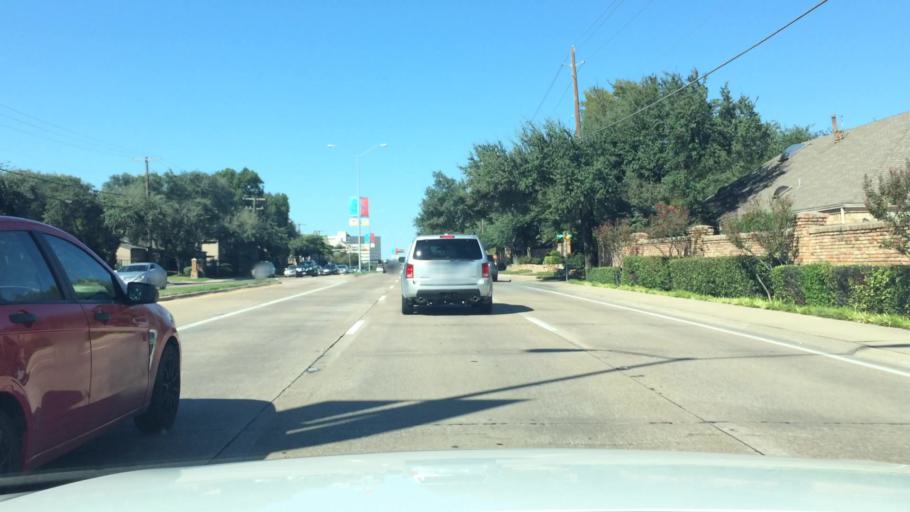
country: US
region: Texas
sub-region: Dallas County
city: Addison
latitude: 32.9400
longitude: -96.8035
